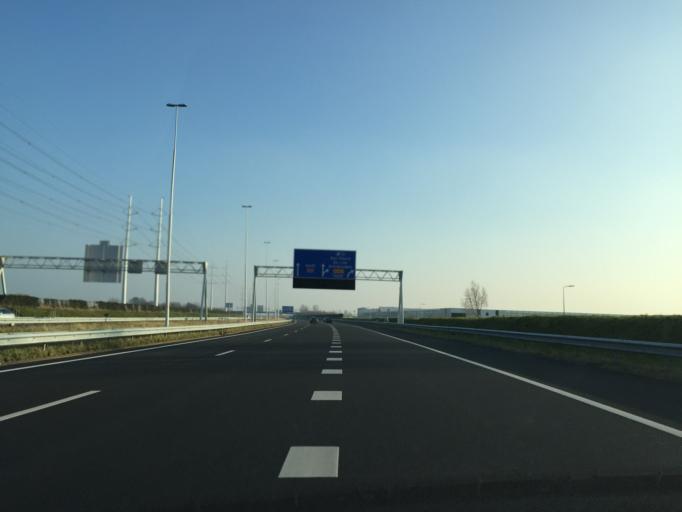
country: NL
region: South Holland
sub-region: Gemeente Rijswijk
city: Rijswijk
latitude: 52.0019
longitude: 4.3120
